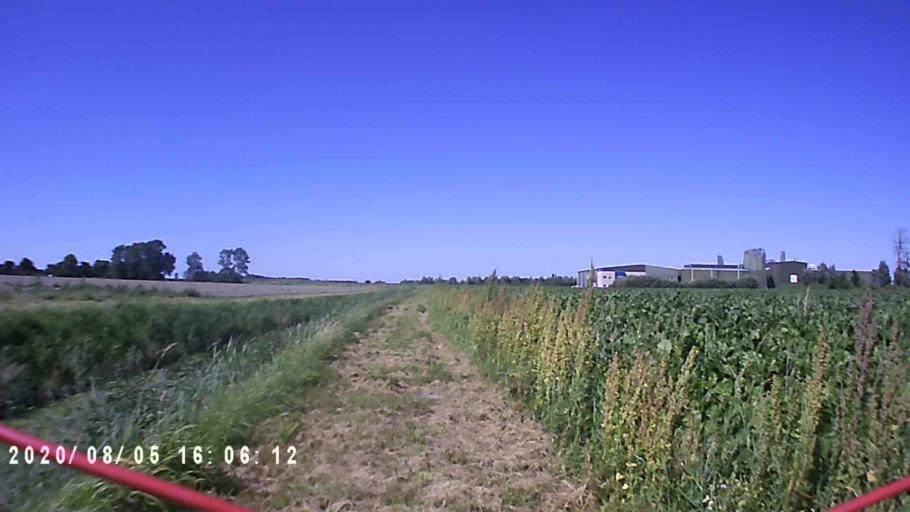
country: NL
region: Groningen
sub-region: Gemeente Winsum
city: Winsum
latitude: 53.3923
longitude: 6.5240
